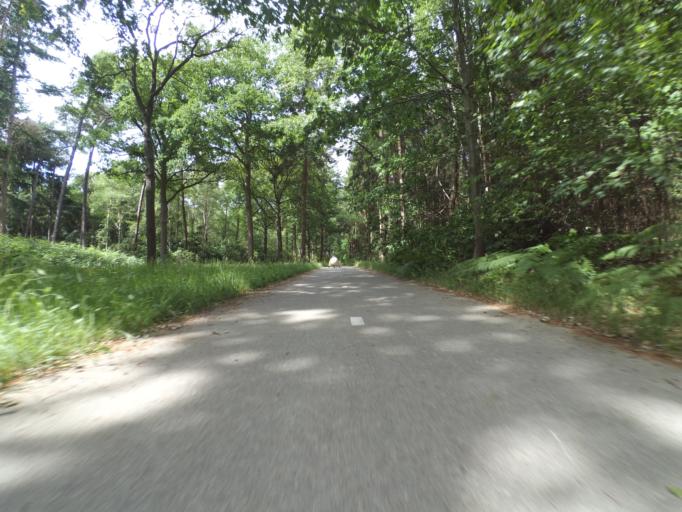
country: BE
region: Flanders
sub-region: Provincie Antwerpen
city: Essen
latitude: 51.4608
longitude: 4.3851
